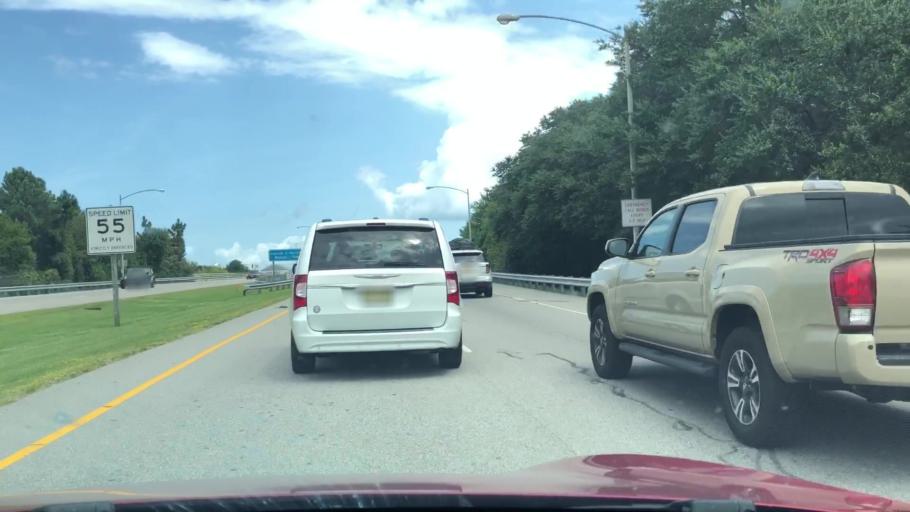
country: US
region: Virginia
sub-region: City of Virginia Beach
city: Virginia Beach
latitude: 36.9155
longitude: -76.1308
